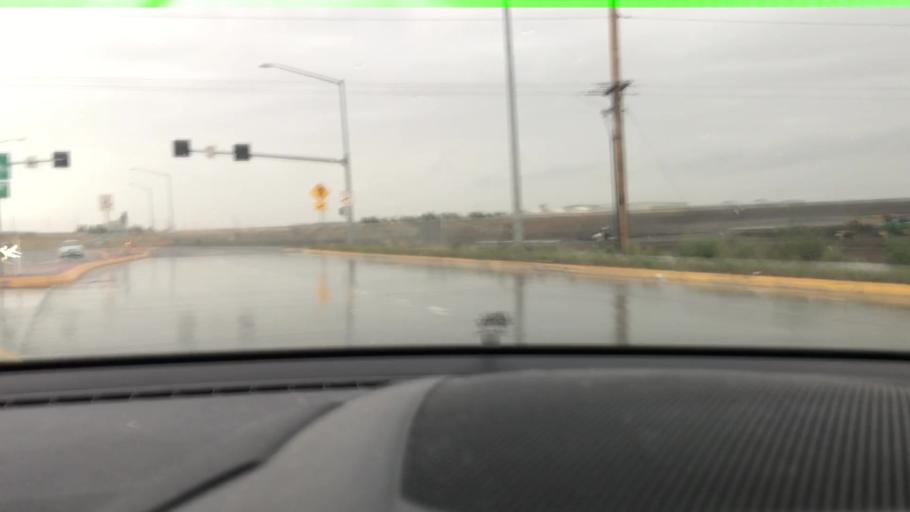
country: US
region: Montana
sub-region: Gallatin County
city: Belgrade
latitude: 45.7612
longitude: -111.1621
